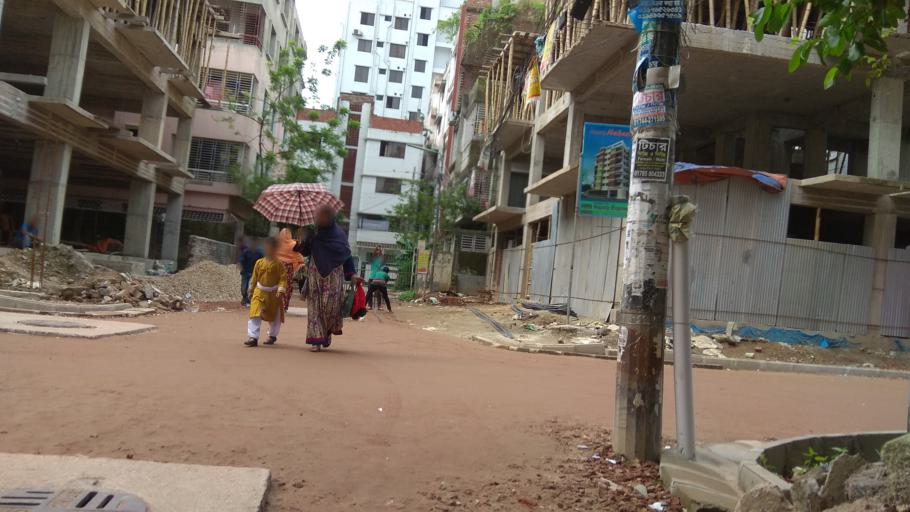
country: BD
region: Dhaka
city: Azimpur
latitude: 23.8146
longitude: 90.3544
